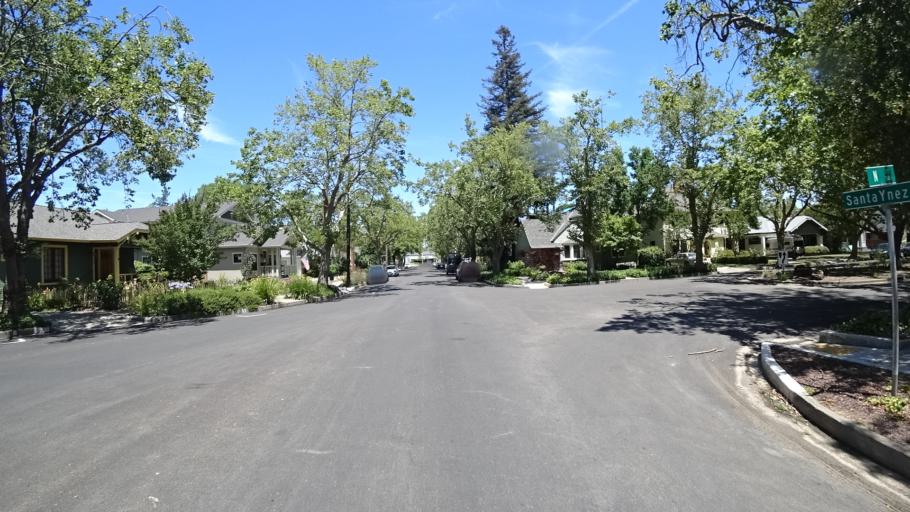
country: US
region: California
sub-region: Sacramento County
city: Sacramento
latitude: 38.5673
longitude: -121.4608
